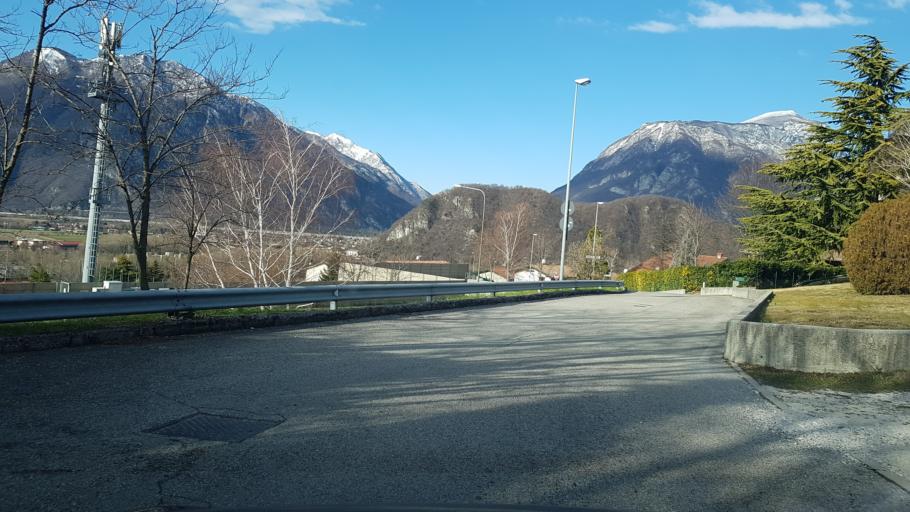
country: IT
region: Friuli Venezia Giulia
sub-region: Provincia di Udine
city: Gemona
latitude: 46.2857
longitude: 13.1350
